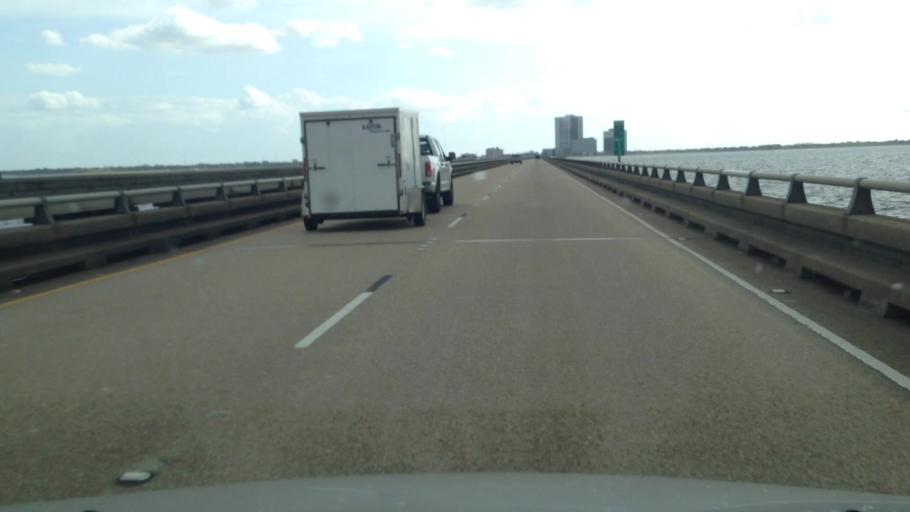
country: US
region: Louisiana
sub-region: Jefferson Parish
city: Metairie
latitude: 30.0436
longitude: -90.1504
